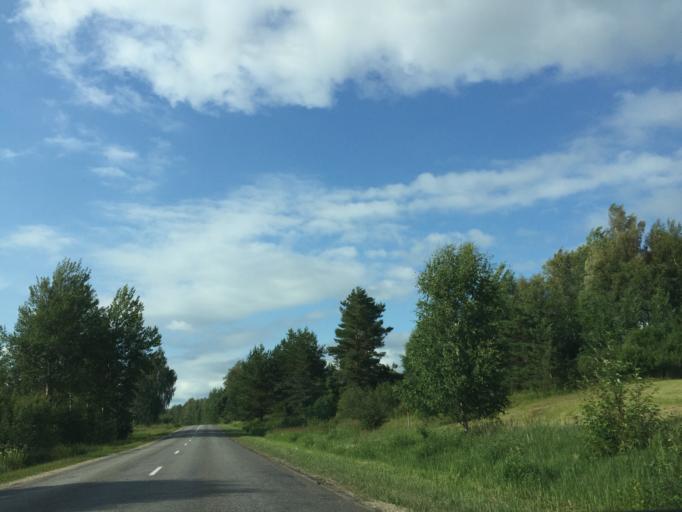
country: LV
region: Dagda
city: Dagda
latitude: 56.3427
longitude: 27.5118
